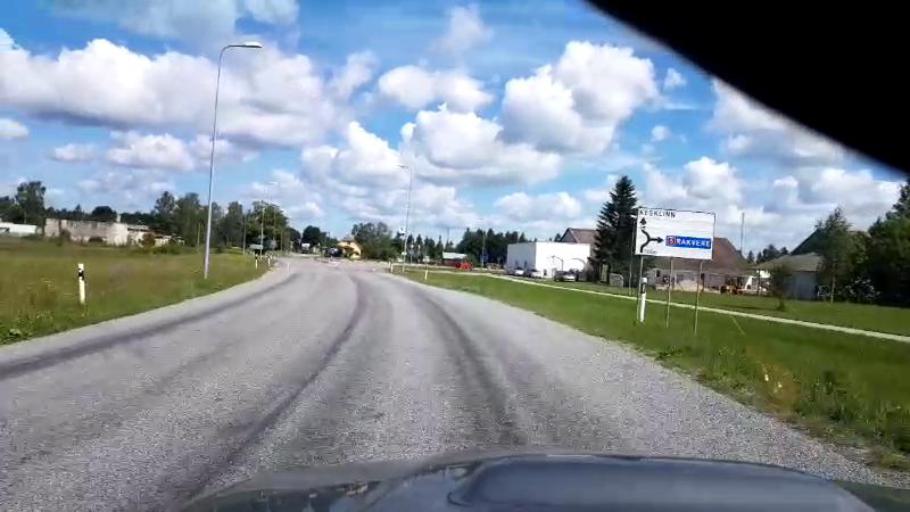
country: EE
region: Laeaene-Virumaa
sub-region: Tapa vald
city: Tapa
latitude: 59.2561
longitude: 25.9423
